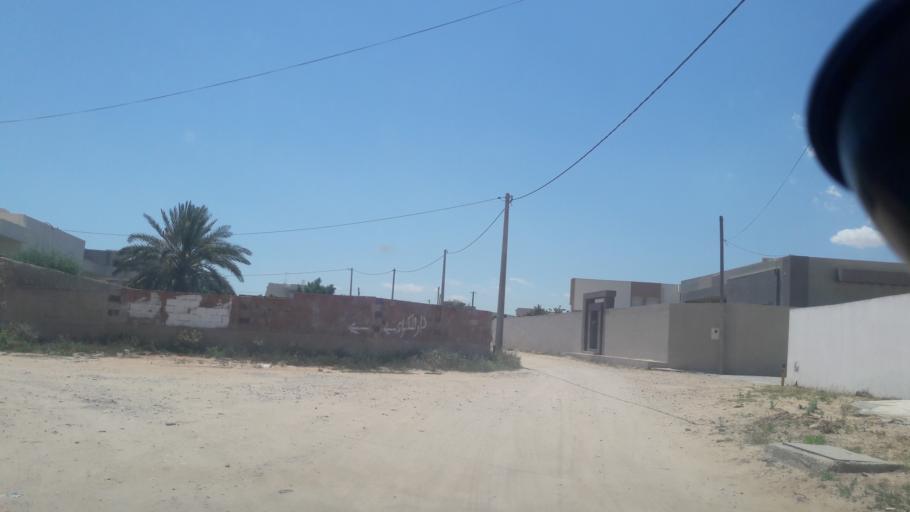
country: TN
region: Safaqis
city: Al Qarmadah
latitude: 34.8072
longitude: 10.7472
